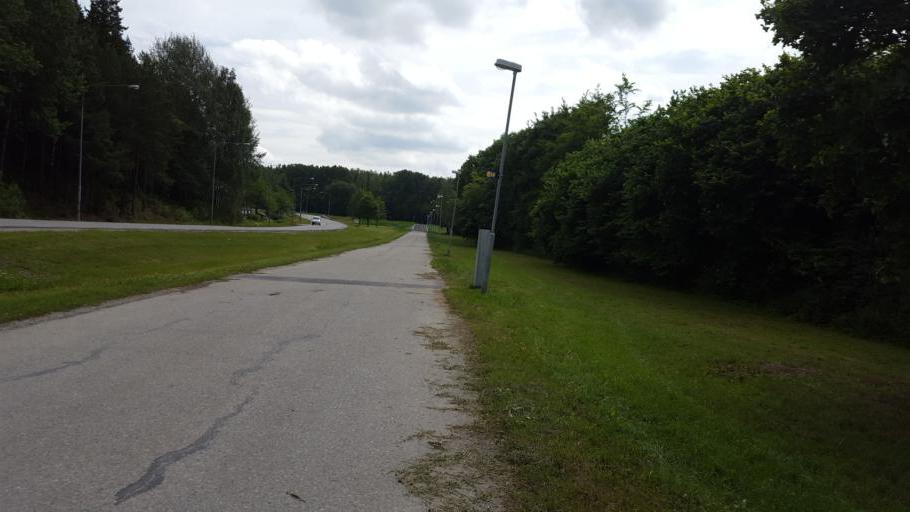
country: SE
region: Stockholm
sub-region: Upplands Vasby Kommun
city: Upplands Vaesby
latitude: 59.5093
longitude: 17.9002
